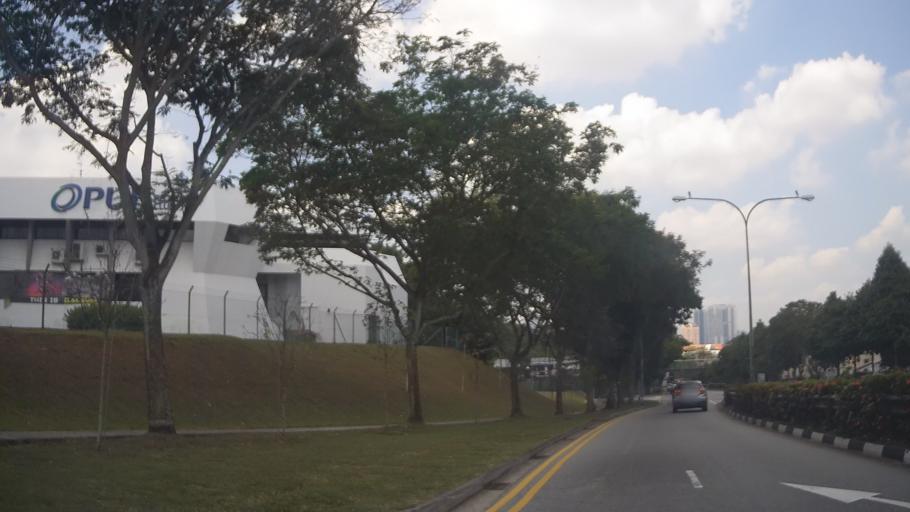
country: SG
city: Singapore
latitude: 1.3428
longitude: 103.8686
